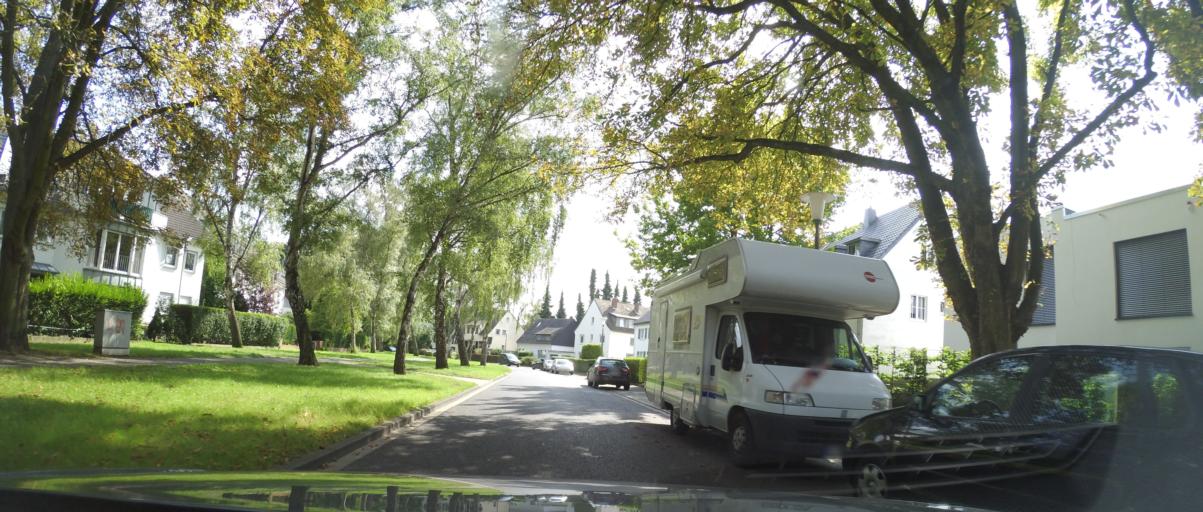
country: DE
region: North Rhine-Westphalia
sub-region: Regierungsbezirk Koln
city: Mengenich
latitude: 50.9352
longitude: 6.8598
